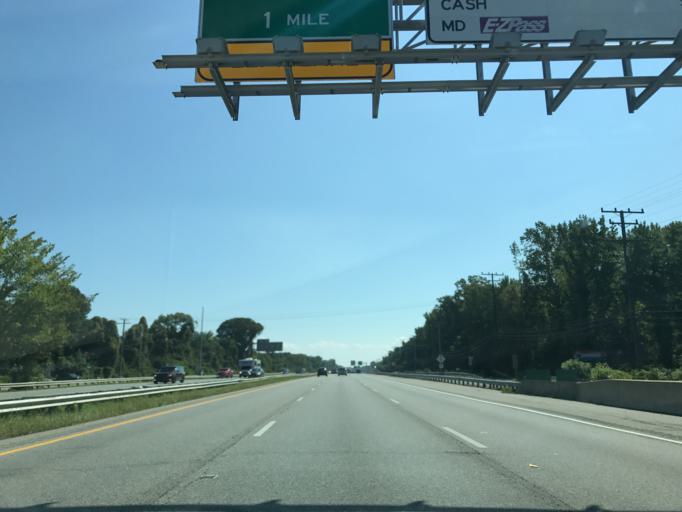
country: US
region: Maryland
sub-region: Anne Arundel County
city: Cape Saint Claire
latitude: 39.0252
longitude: -76.4352
